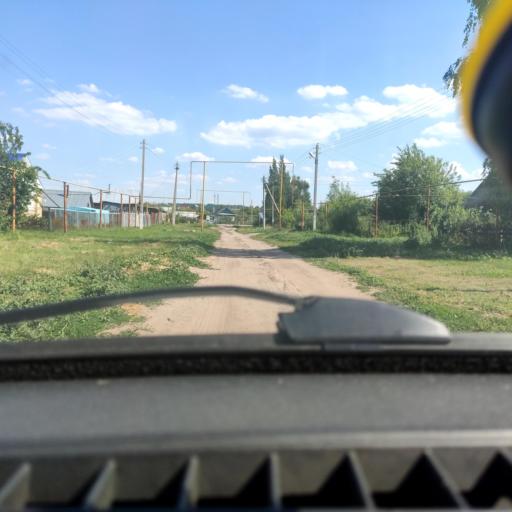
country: RU
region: Samara
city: Povolzhskiy
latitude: 53.7555
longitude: 49.7341
